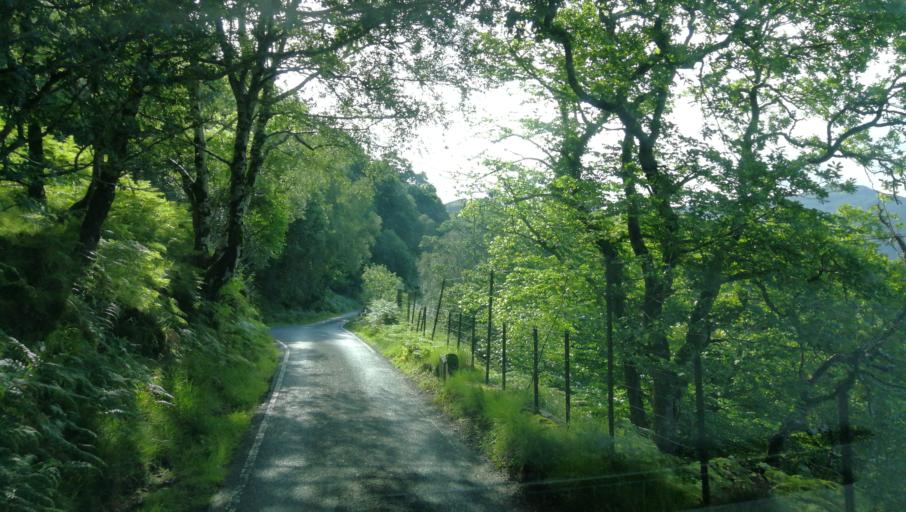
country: GB
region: Scotland
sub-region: Argyll and Bute
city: Isle Of Mull
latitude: 56.6812
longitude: -5.8588
